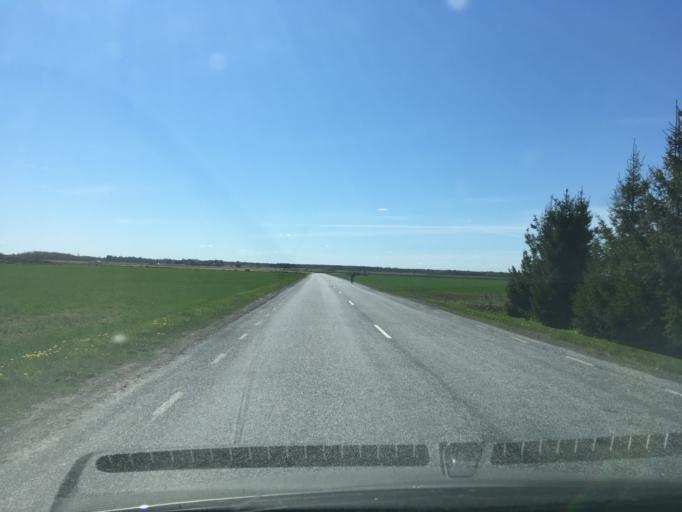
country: EE
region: Harju
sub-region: Raasiku vald
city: Arukula
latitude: 59.4295
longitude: 25.0801
